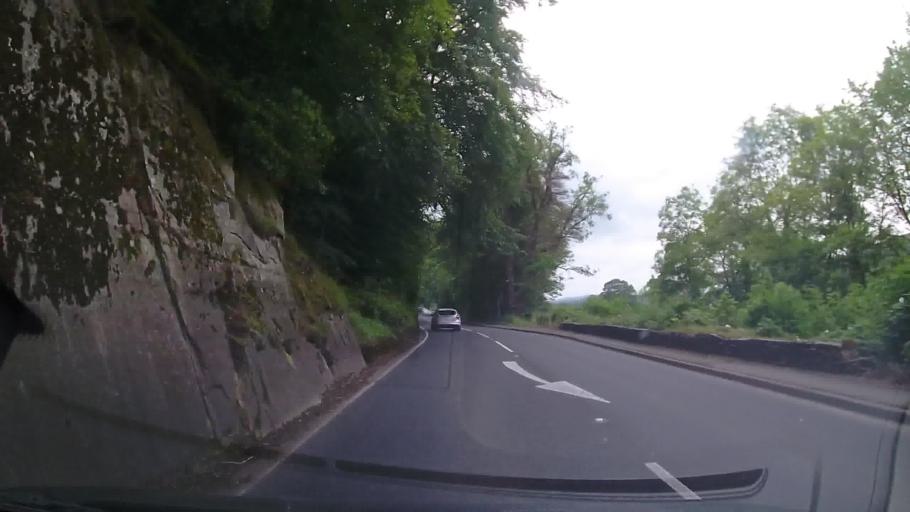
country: GB
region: Wales
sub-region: Denbighshire
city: Corwen
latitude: 52.9811
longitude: -3.3474
